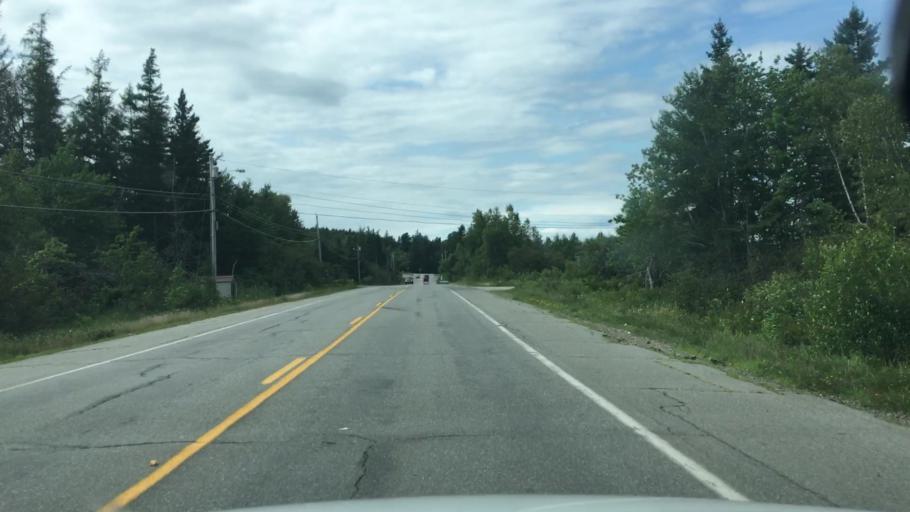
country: US
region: Maine
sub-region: Washington County
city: Eastport
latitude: 44.9679
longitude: -67.0700
